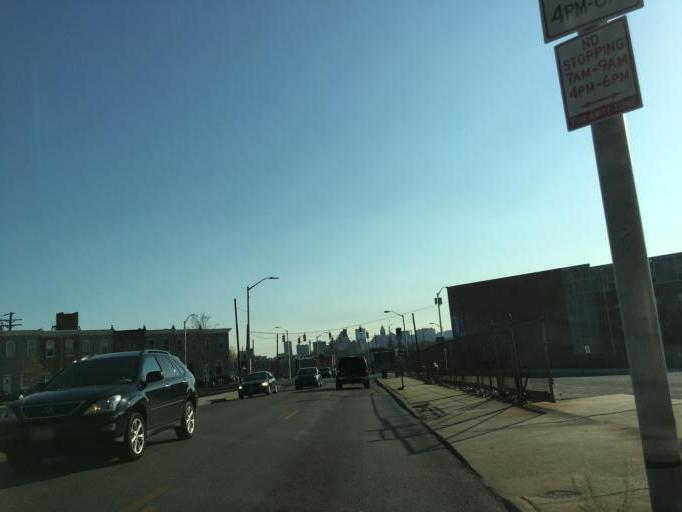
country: US
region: Maryland
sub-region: City of Baltimore
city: Baltimore
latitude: 39.3094
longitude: -76.5879
